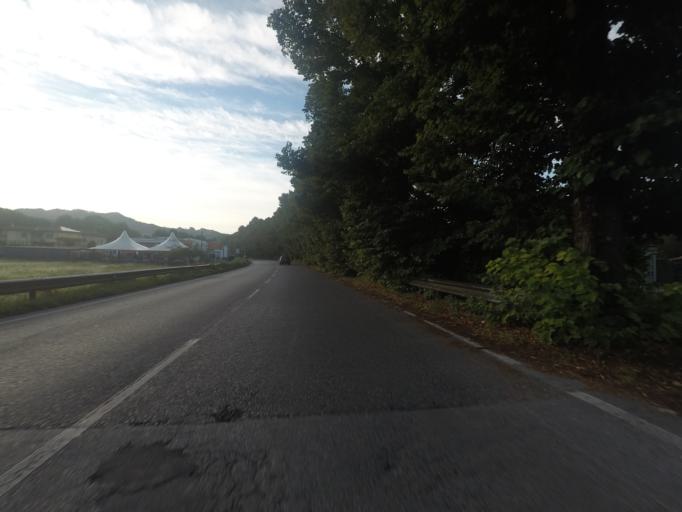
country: IT
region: Tuscany
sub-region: Provincia di Lucca
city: Corsanico-Bargecchia
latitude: 43.9302
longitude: 10.3120
